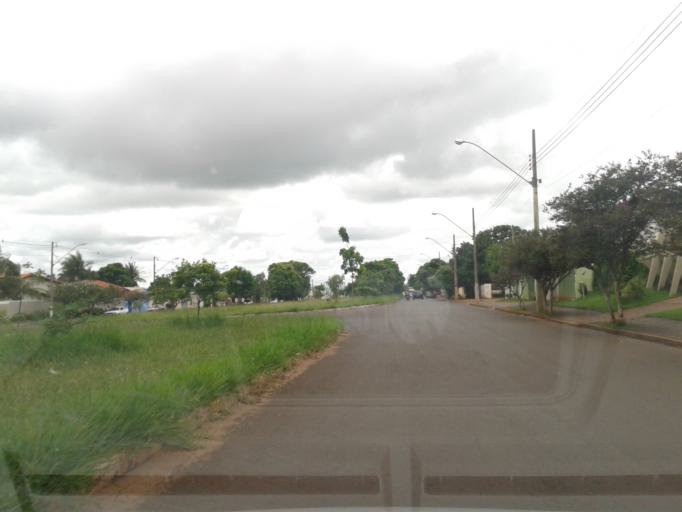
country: BR
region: Minas Gerais
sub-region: Ituiutaba
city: Ituiutaba
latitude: -18.9886
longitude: -49.4608
